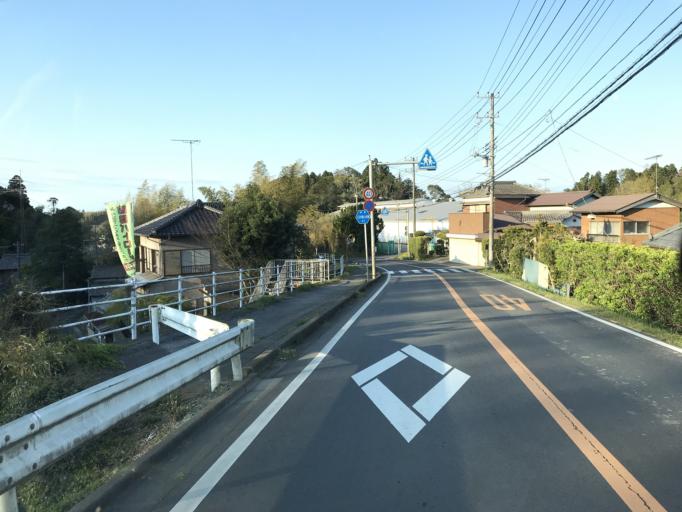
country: JP
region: Chiba
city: Yokaichiba
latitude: 35.7459
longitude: 140.5577
